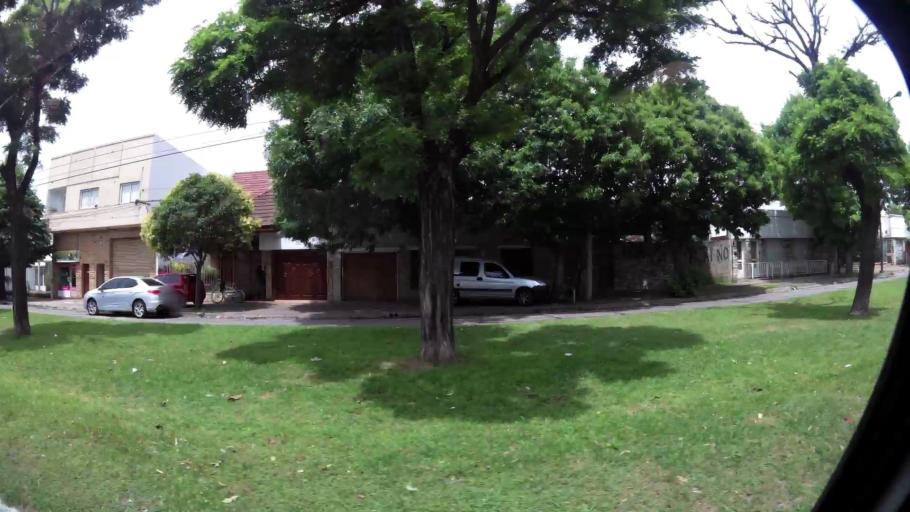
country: AR
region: Buenos Aires
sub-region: Partido de La Plata
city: La Plata
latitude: -34.9469
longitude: -57.9578
